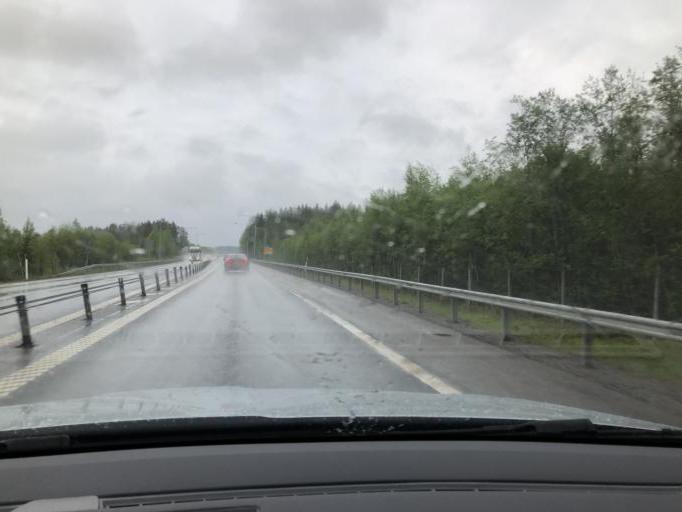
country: SE
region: Vaesterbotten
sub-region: Umea Kommun
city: Roback
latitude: 63.7524
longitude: 20.1533
